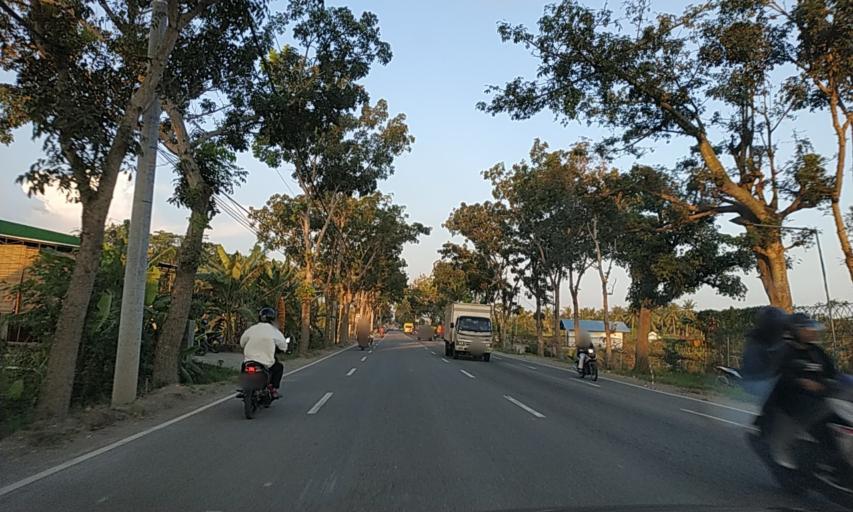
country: ID
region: Daerah Istimewa Yogyakarta
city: Srandakan
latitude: -7.8864
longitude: 110.0665
